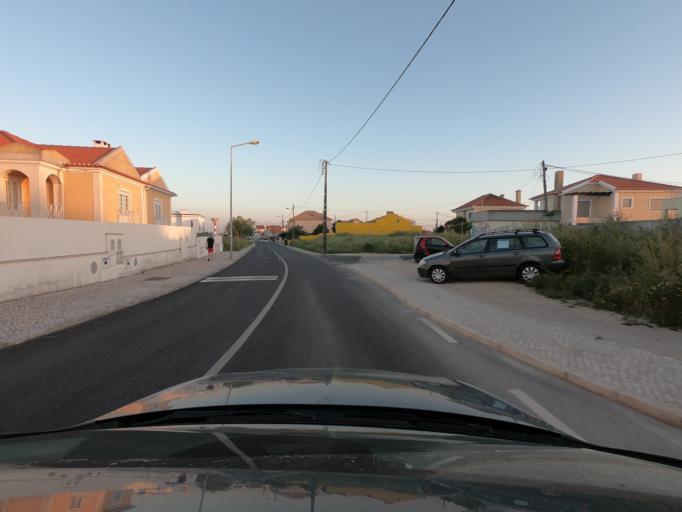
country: PT
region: Lisbon
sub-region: Cascais
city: Sao Domingos de Rana
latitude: 38.7267
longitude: -9.3432
